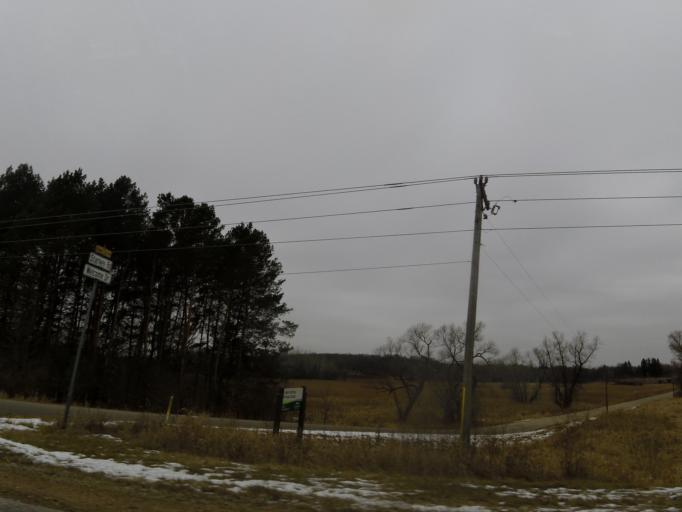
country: US
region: Minnesota
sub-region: Hennepin County
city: Orono
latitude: 44.9952
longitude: -93.6145
